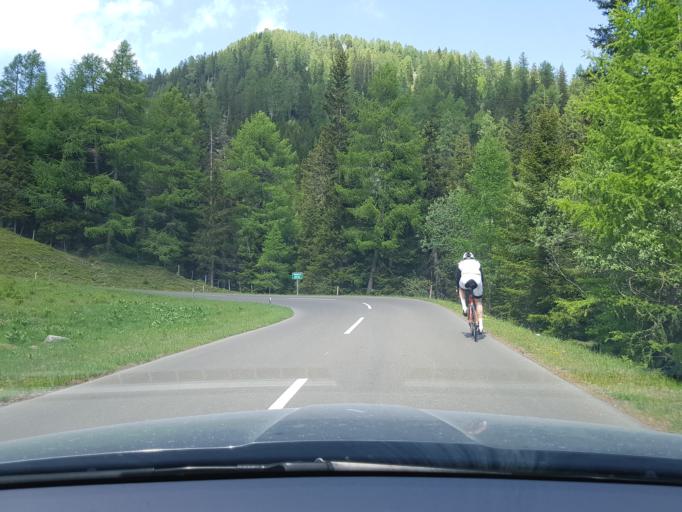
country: AT
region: Salzburg
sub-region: Politischer Bezirk Tamsweg
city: Thomatal
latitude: 46.9557
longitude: 13.7284
